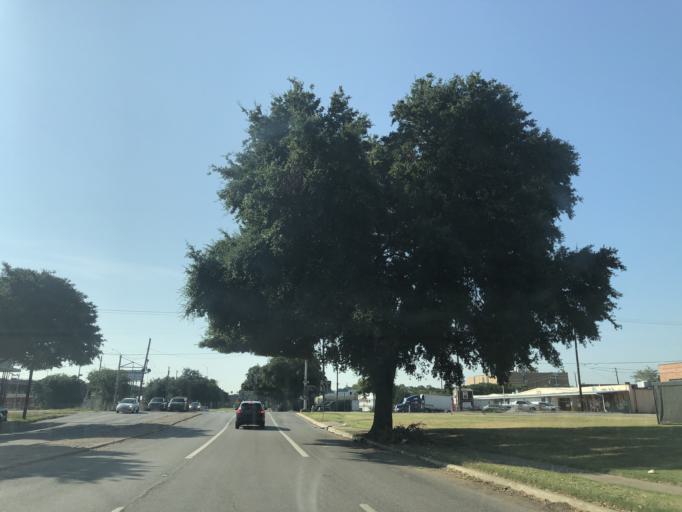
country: US
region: Texas
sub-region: Dallas County
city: Dallas
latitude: 32.7692
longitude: -96.7797
